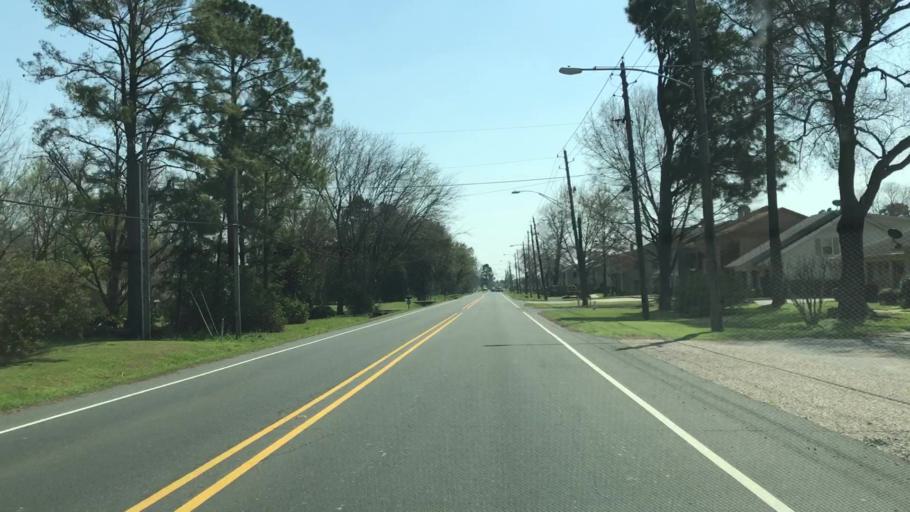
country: US
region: Louisiana
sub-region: Bossier Parish
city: Bossier City
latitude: 32.4134
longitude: -93.6922
